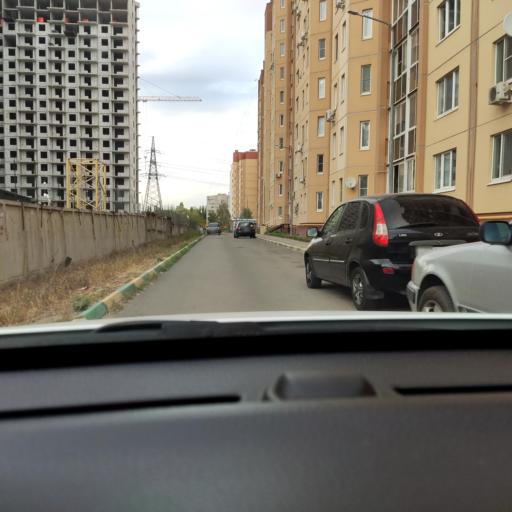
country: RU
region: Voronezj
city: Voronezh
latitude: 51.7170
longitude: 39.2630
